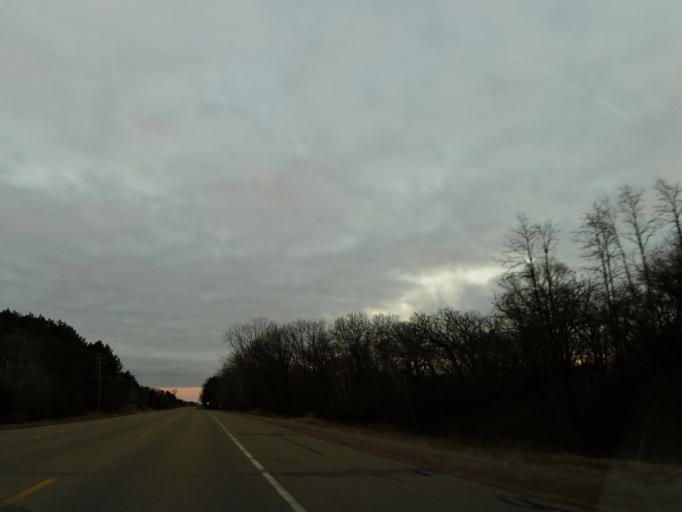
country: US
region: Minnesota
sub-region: Washington County
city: Grant
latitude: 45.0578
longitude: -92.9097
